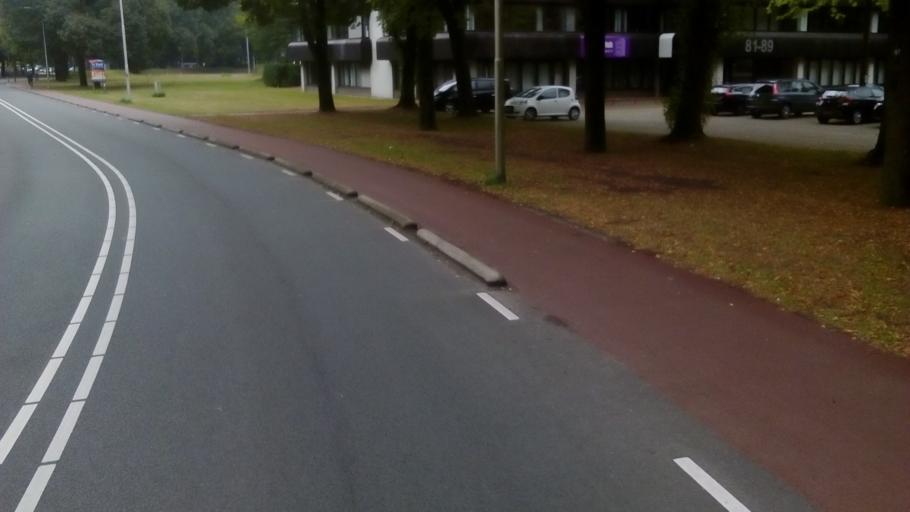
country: NL
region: North Brabant
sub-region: Gemeente Goirle
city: Goirle
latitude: 51.5433
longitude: 5.0533
